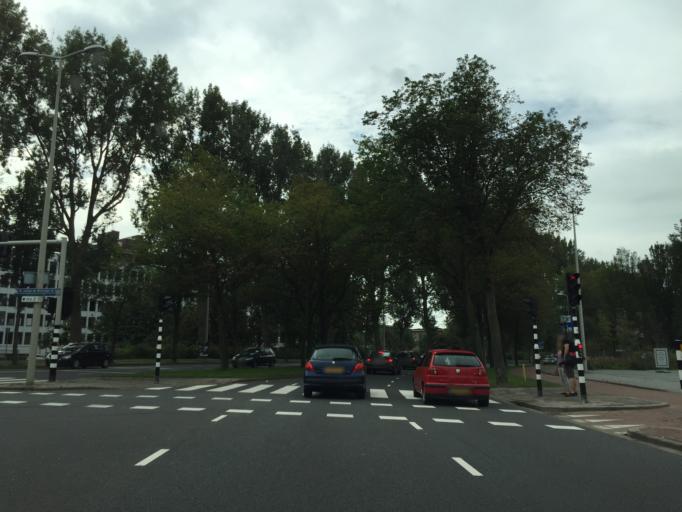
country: NL
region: South Holland
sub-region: Gemeente Den Haag
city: Scheveningen
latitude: 52.0895
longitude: 4.2830
